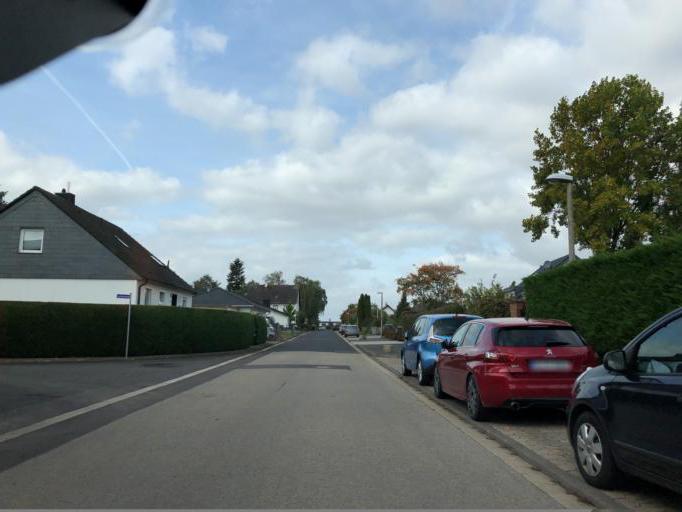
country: DE
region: North Rhine-Westphalia
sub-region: Regierungsbezirk Koln
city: Rheinbach
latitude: 50.6491
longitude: 6.9170
